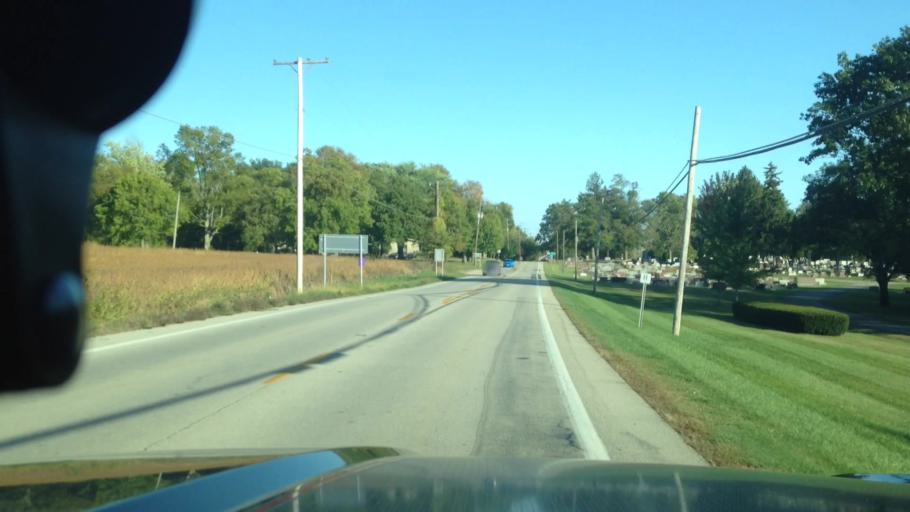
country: US
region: Ohio
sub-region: Darke County
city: Greenville
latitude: 40.1097
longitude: -84.6462
